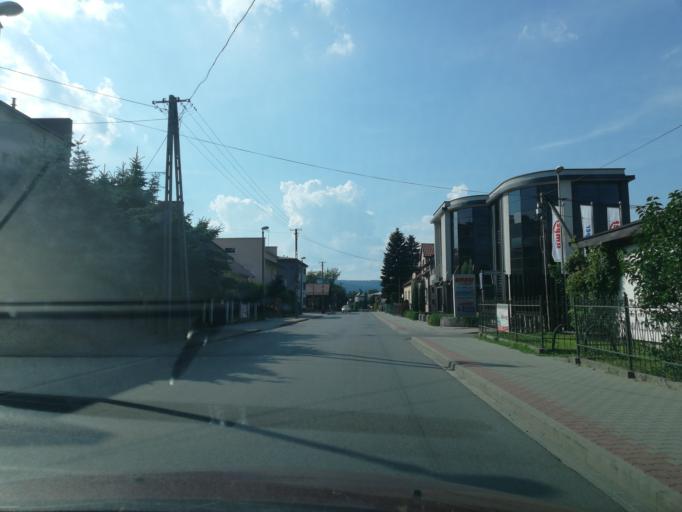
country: PL
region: Lesser Poland Voivodeship
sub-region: Powiat nowosadecki
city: Nowy Sacz
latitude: 49.6293
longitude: 20.6997
